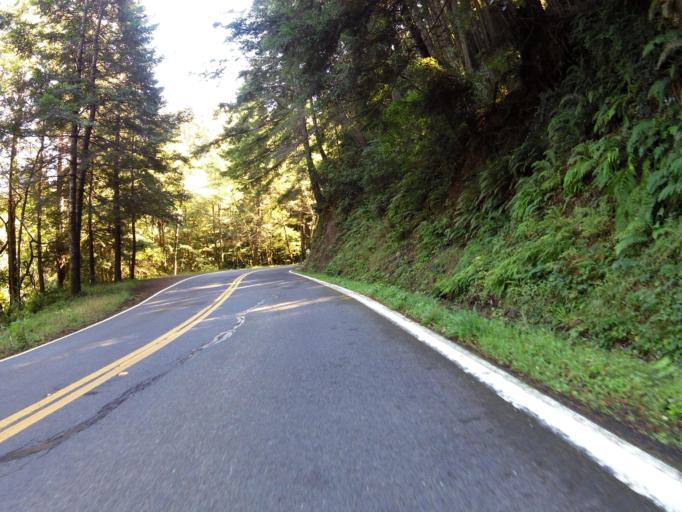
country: US
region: California
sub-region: Mendocino County
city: Fort Bragg
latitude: 39.7356
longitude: -123.8132
